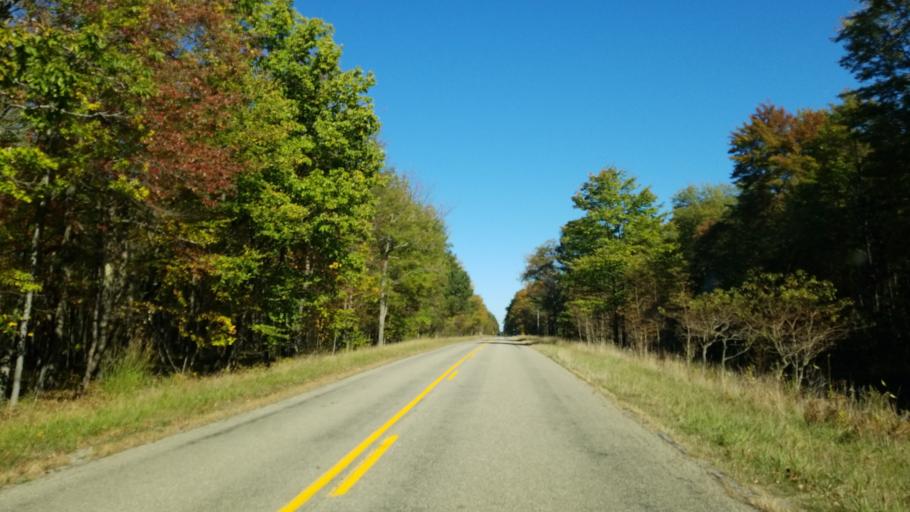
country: US
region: Pennsylvania
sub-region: Clearfield County
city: Shiloh
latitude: 41.2564
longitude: -78.3225
